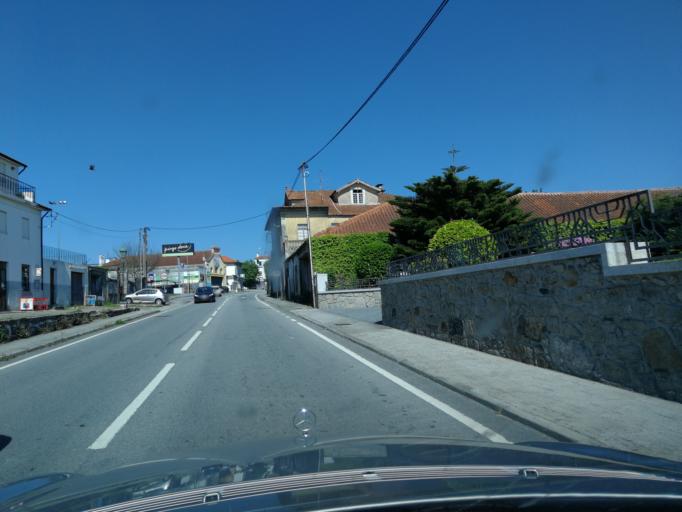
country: PT
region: Viana do Castelo
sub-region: Viana do Castelo
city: Meadela
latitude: 41.7084
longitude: -8.7773
